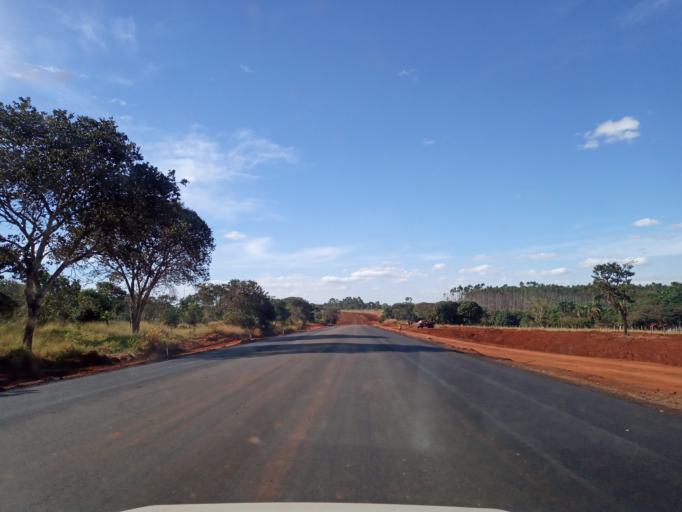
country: BR
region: Minas Gerais
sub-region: Ituiutaba
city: Ituiutaba
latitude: -18.9812
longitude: -49.5089
